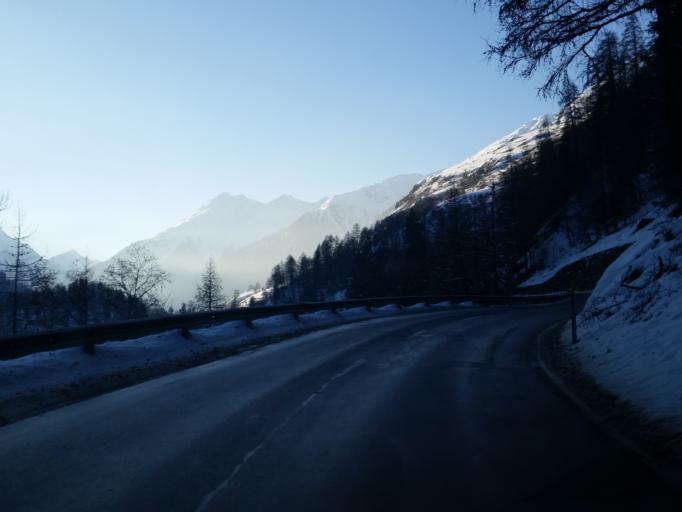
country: CH
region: Grisons
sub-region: Inn District
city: Zernez
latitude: 46.7716
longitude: 10.1653
